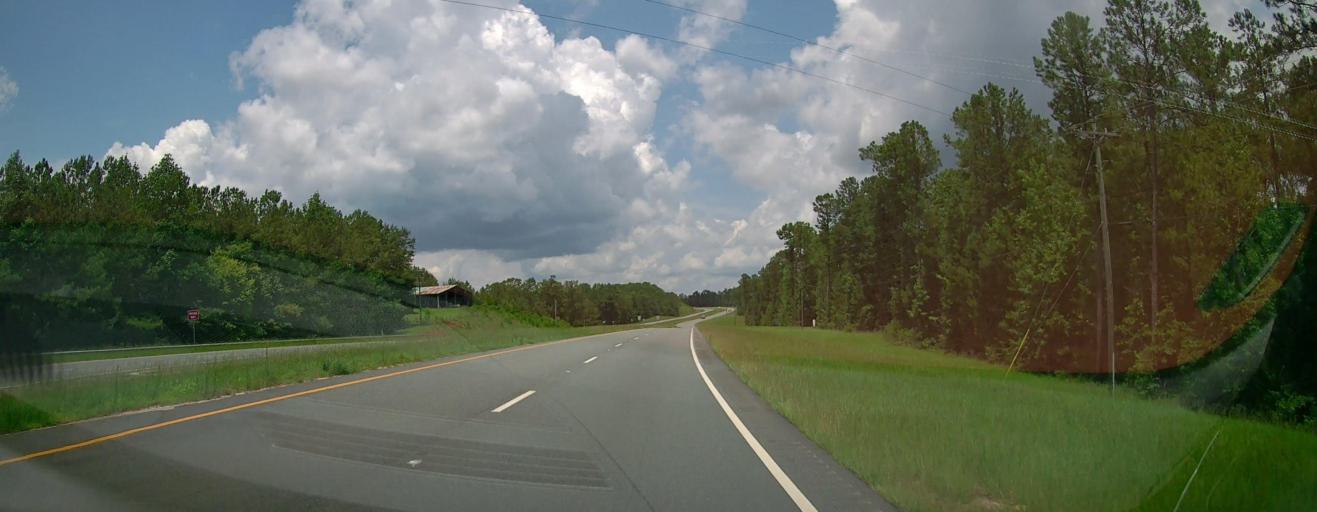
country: US
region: Georgia
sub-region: Upson County
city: Thomaston
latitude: 32.8094
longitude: -84.2837
